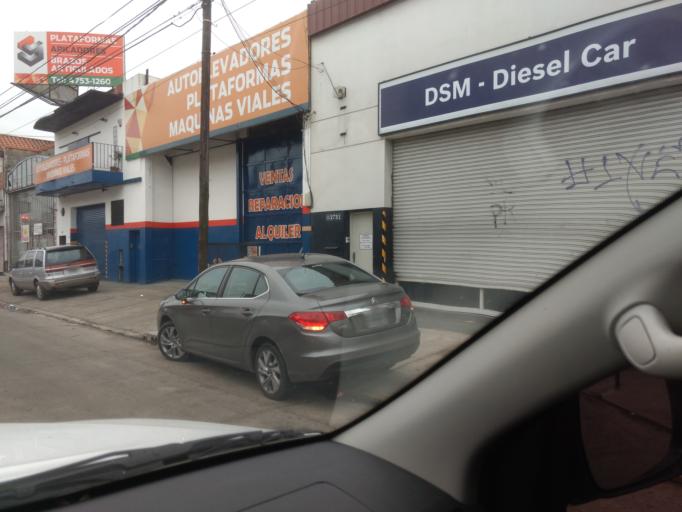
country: AR
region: Buenos Aires
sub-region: Partido de General San Martin
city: General San Martin
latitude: -34.5747
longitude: -58.5491
